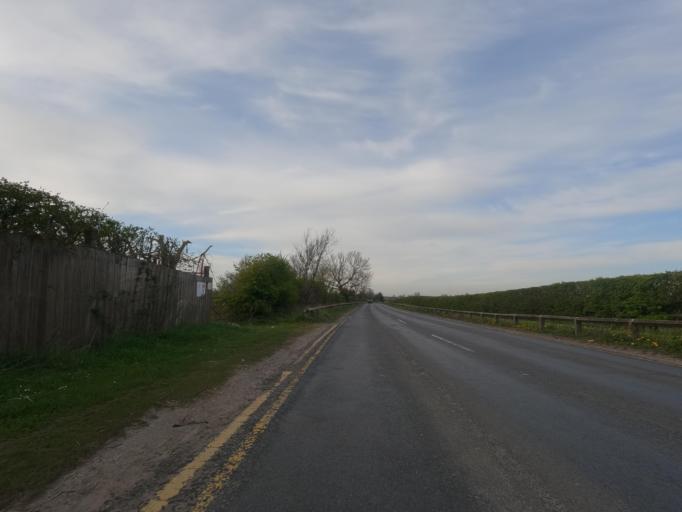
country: GB
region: England
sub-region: Newcastle upon Tyne
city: Dinnington
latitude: 55.0452
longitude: -1.6706
